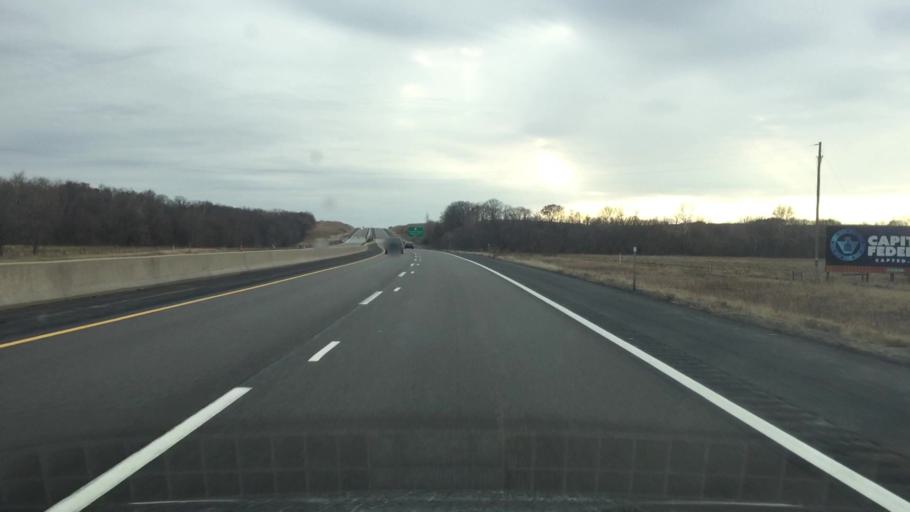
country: US
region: Kansas
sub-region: Osage County
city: Osage City
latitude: 38.6668
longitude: -96.0172
